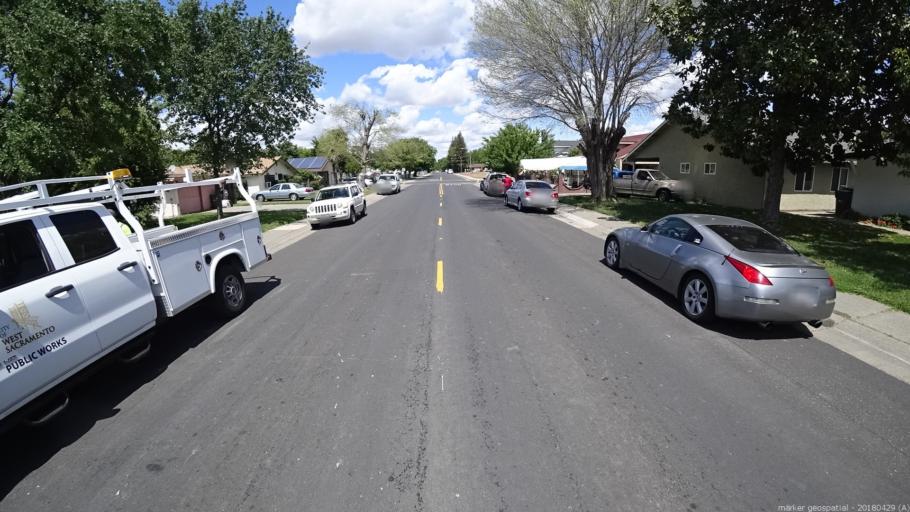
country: US
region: California
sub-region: Yolo County
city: West Sacramento
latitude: 38.5931
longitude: -121.5199
